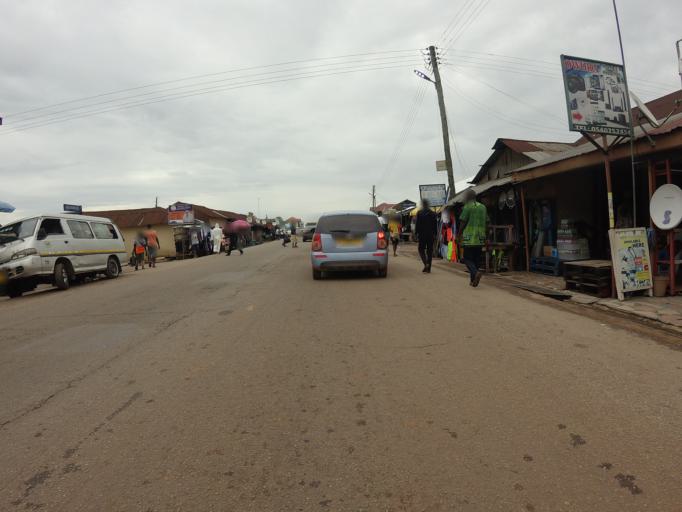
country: GH
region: Eastern
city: Begoro
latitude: 6.3802
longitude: -0.5486
